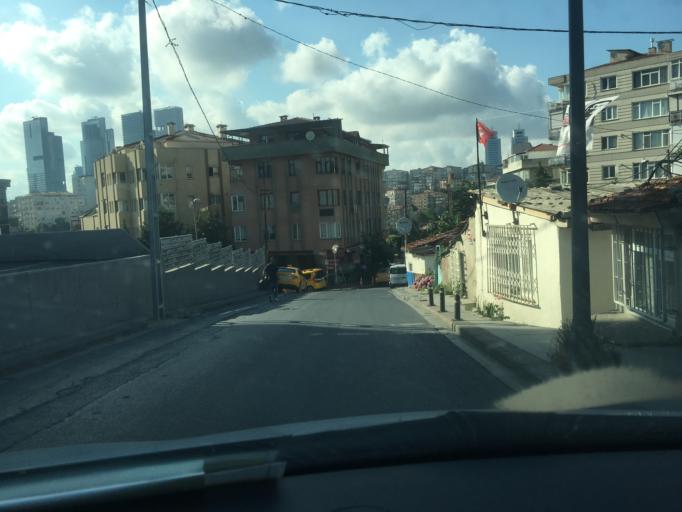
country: TR
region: Istanbul
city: Sisli
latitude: 41.0588
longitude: 29.0082
